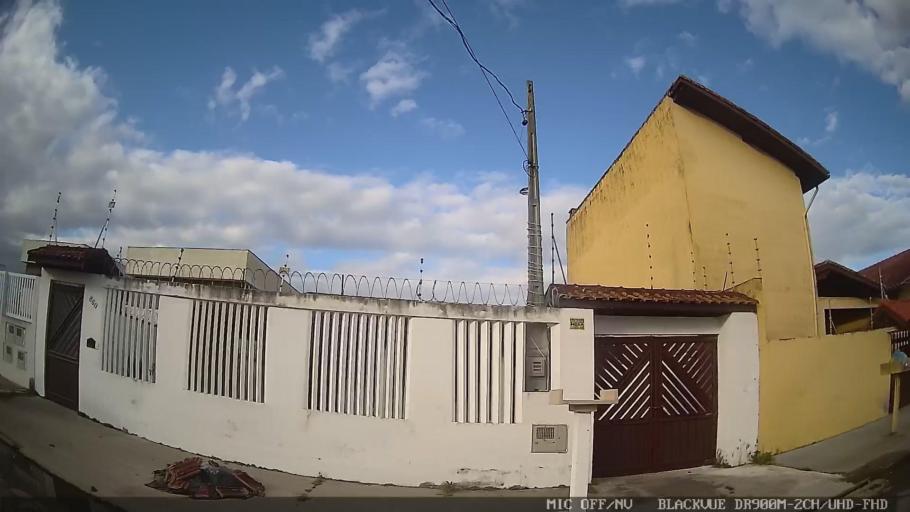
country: BR
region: Sao Paulo
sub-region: Itanhaem
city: Itanhaem
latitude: -24.2055
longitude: -46.8415
